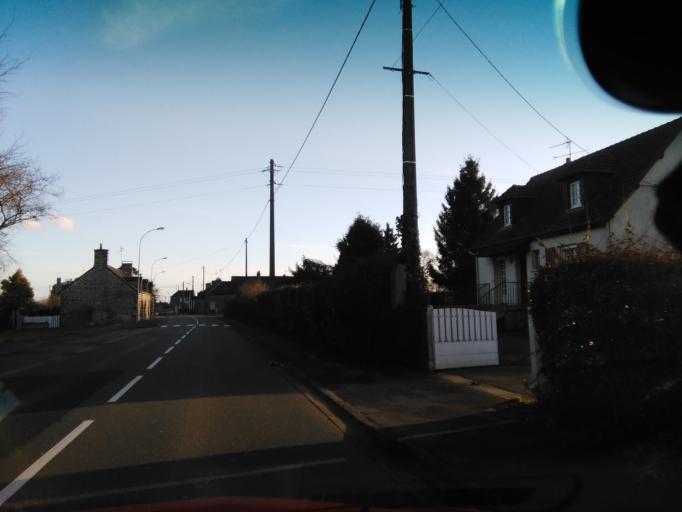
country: FR
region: Lower Normandy
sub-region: Departement de l'Orne
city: La Ferte-Mace
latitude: 48.6035
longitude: -0.3590
